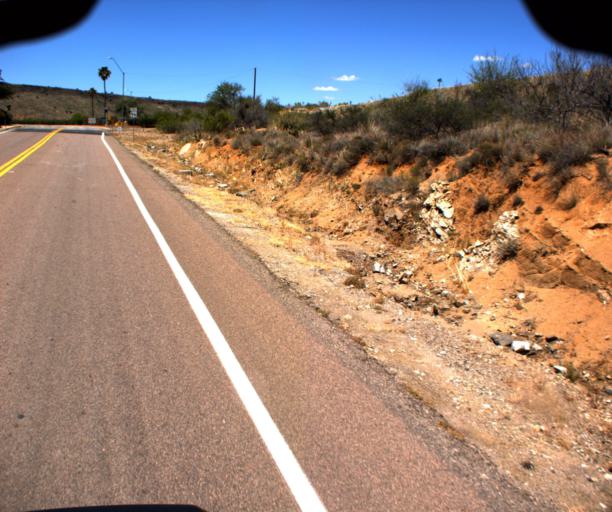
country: US
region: Arizona
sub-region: Yavapai County
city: Bagdad
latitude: 34.5678
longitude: -113.1754
